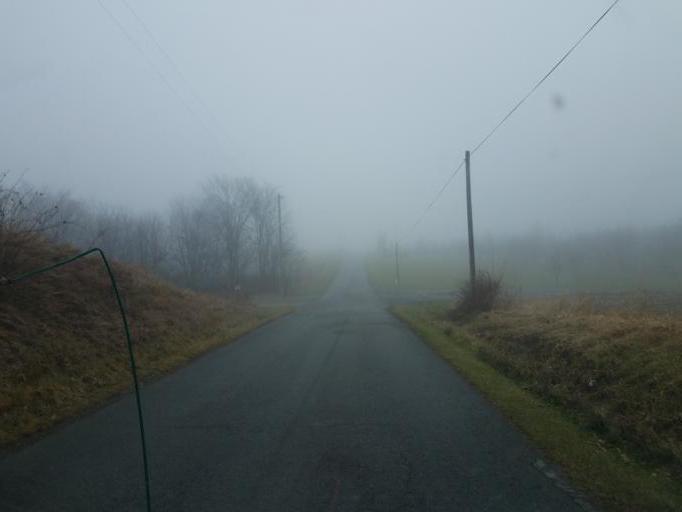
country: US
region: Ohio
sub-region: Champaign County
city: North Lewisburg
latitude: 40.2909
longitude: -83.6297
